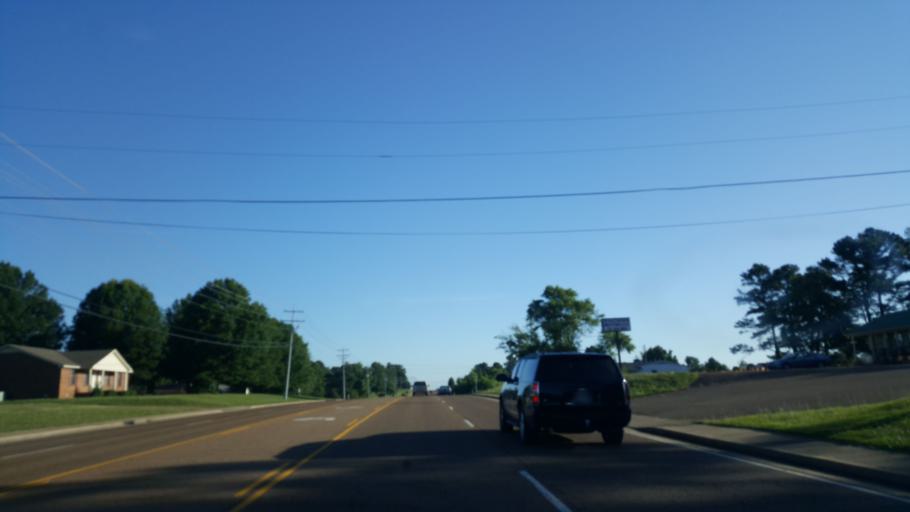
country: US
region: Tennessee
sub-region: Henderson County
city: Lexington
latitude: 35.6795
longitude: -88.3855
